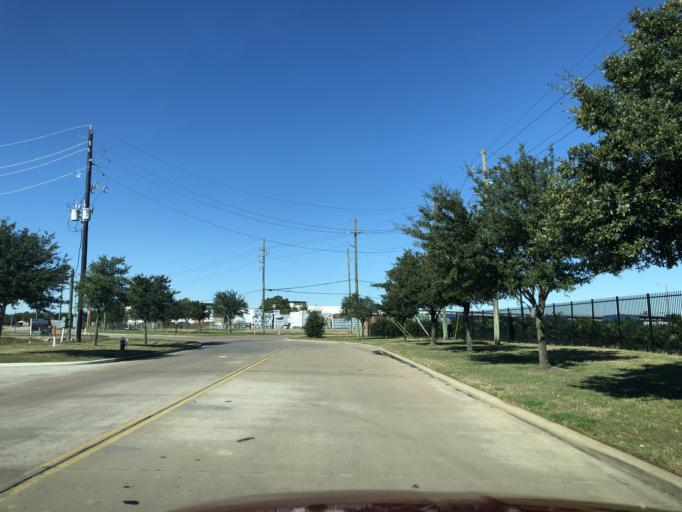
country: US
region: Texas
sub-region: Harris County
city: Oak Cliff Place
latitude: 29.9360
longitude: -95.6543
